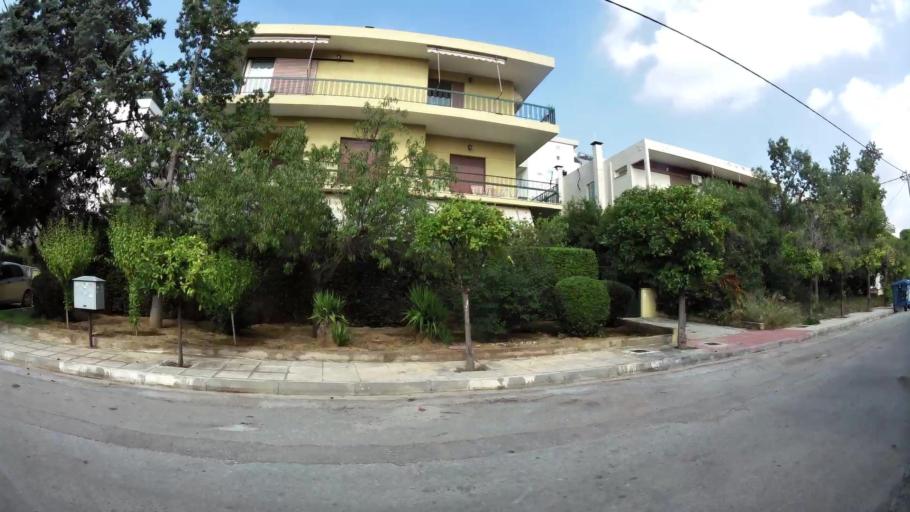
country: GR
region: Attica
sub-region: Nomarchia Athinas
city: Papagou
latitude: 37.9852
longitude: 23.7916
